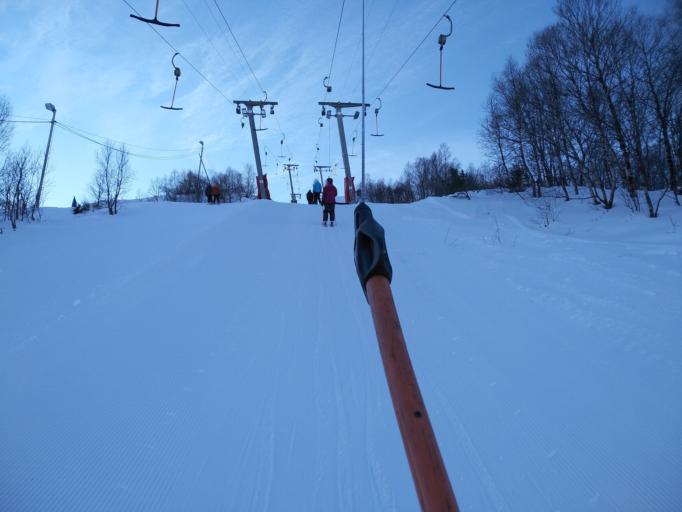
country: NO
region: Rogaland
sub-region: Sauda
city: Sauda
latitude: 59.6202
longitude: 6.2366
